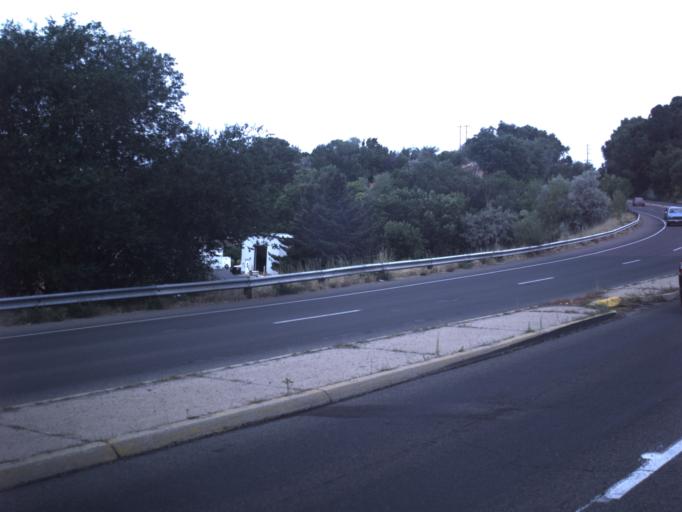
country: US
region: Utah
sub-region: Weber County
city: Ogden
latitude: 41.2434
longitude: -111.9453
